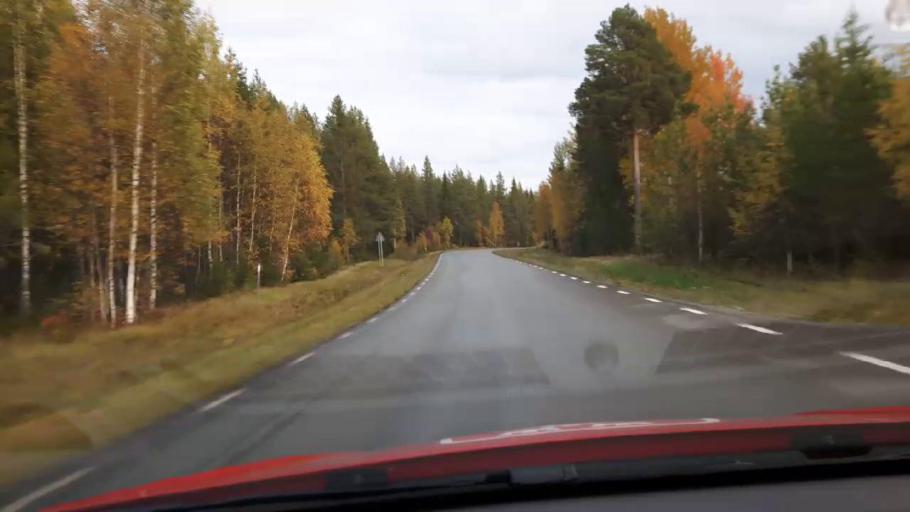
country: SE
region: Jaemtland
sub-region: OEstersunds Kommun
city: Lit
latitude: 63.3173
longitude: 15.0883
